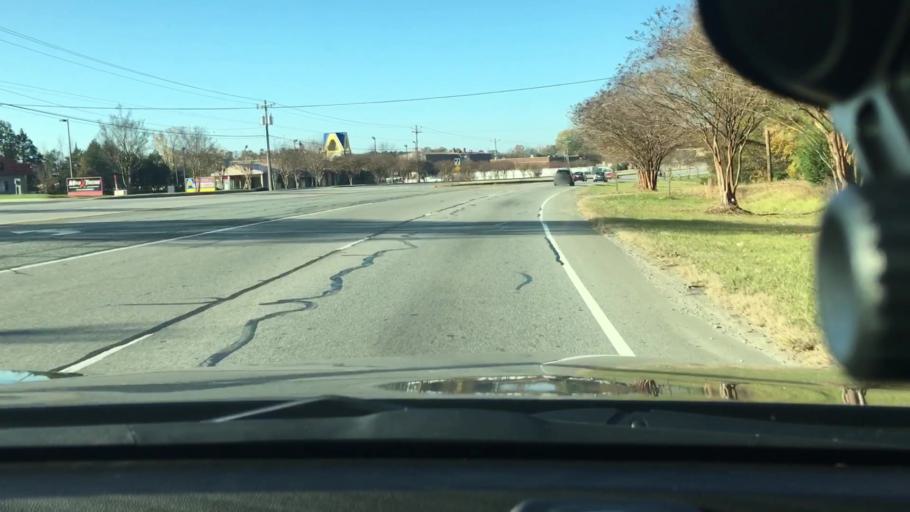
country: US
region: North Carolina
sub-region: Cabarrus County
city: Harrisburg
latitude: 35.3165
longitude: -80.6766
